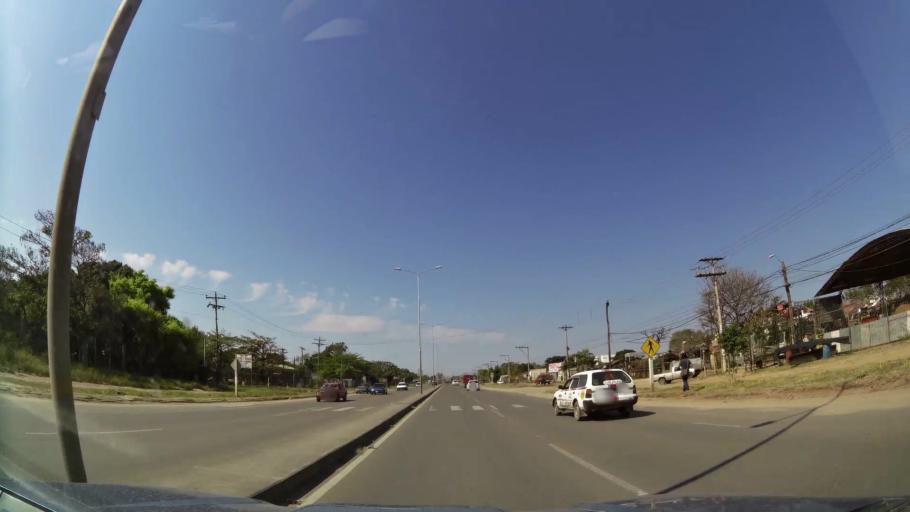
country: BO
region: Santa Cruz
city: Santa Cruz de la Sierra
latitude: -17.7669
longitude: -63.1116
